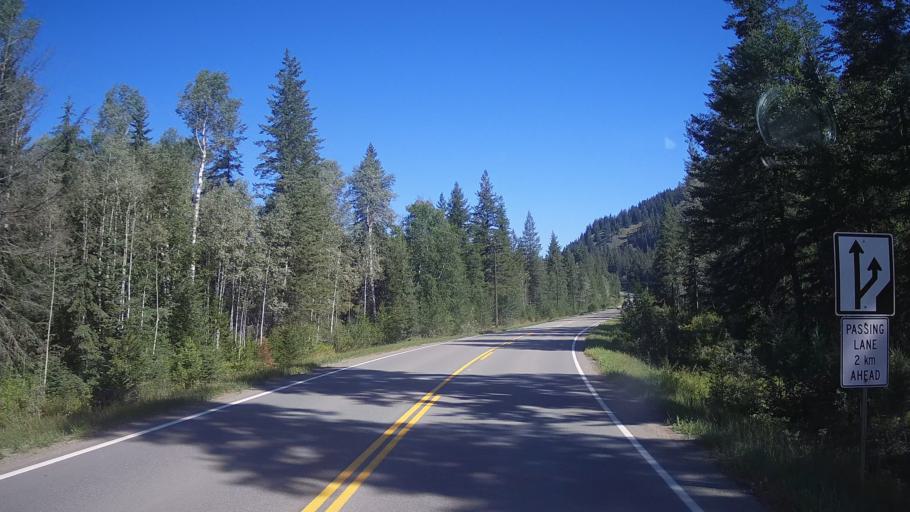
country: CA
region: British Columbia
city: Kamloops
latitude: 51.4416
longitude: -120.2119
